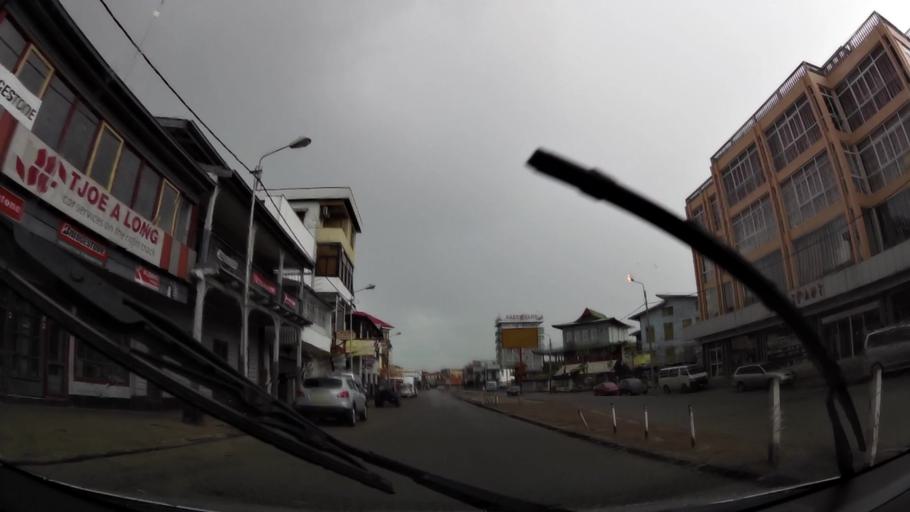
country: SR
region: Paramaribo
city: Paramaribo
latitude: 5.8249
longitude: -55.1626
